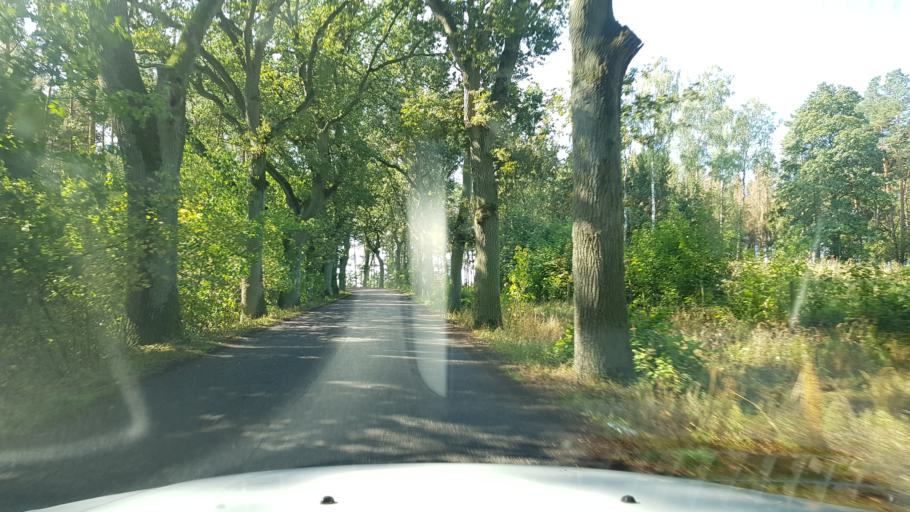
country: PL
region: West Pomeranian Voivodeship
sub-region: Powiat stargardzki
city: Dolice
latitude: 53.2190
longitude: 15.2158
